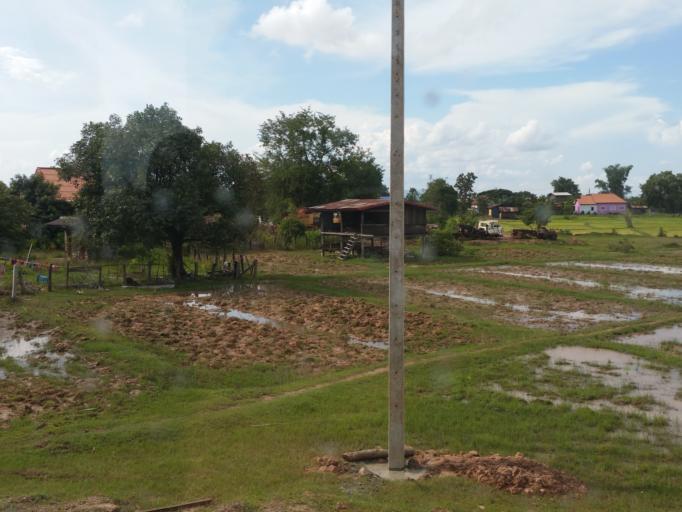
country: LA
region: Champasak
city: Pakxe
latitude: 15.1038
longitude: 105.7610
